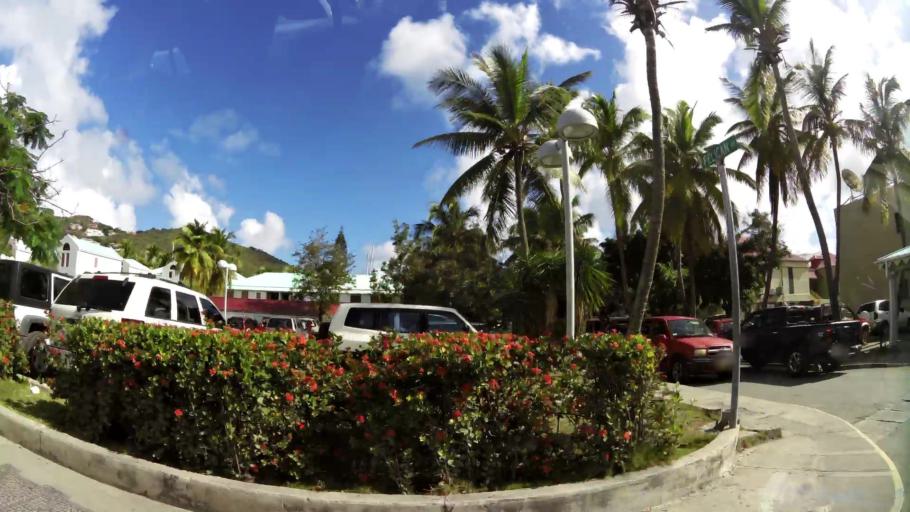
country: VG
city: Road Town
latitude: 18.4228
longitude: -64.6185
